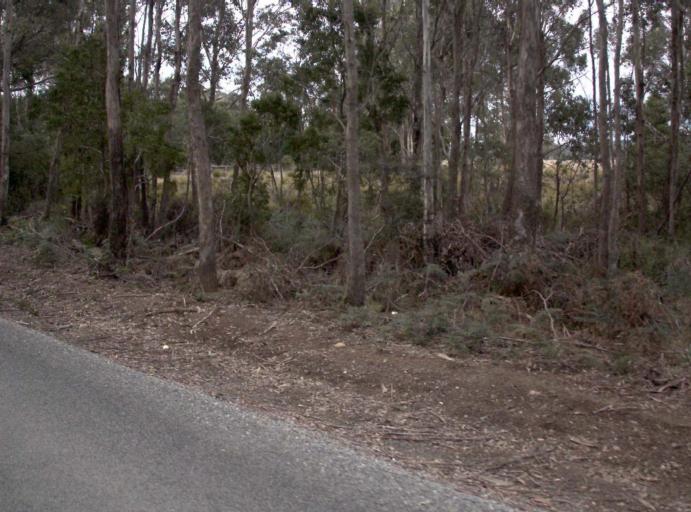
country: AU
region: Tasmania
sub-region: Launceston
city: Newstead
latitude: -41.3679
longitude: 147.2374
